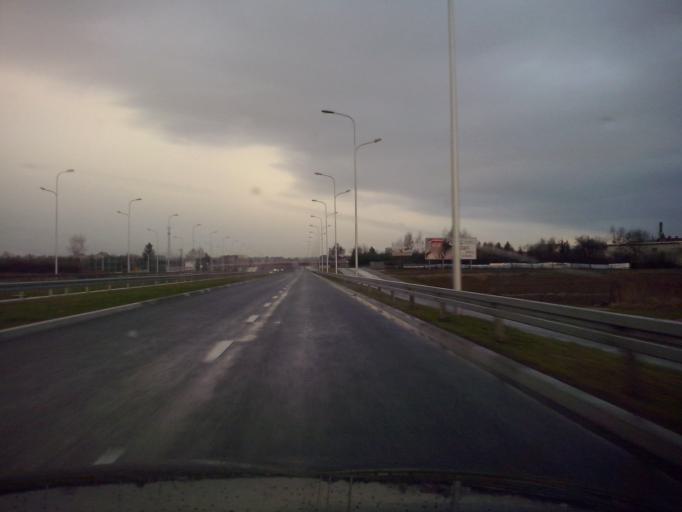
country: PL
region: Lublin Voivodeship
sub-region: Powiat lubelski
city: Jastkow
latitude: 51.2701
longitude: 22.4836
